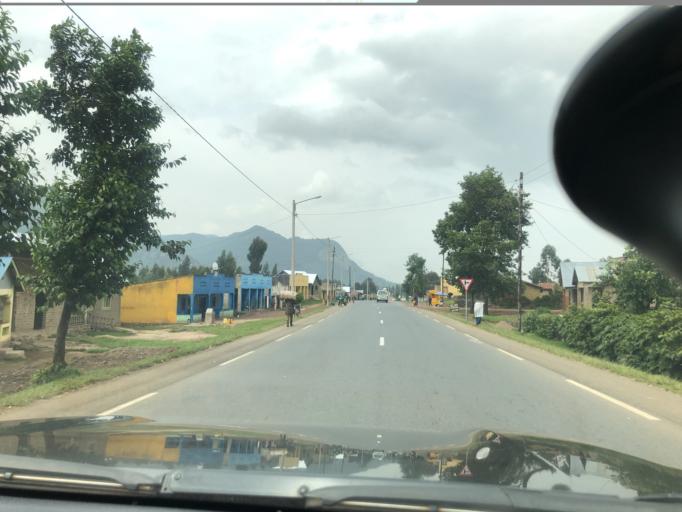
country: RW
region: Western Province
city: Gisenyi
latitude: -1.6333
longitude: 29.4124
